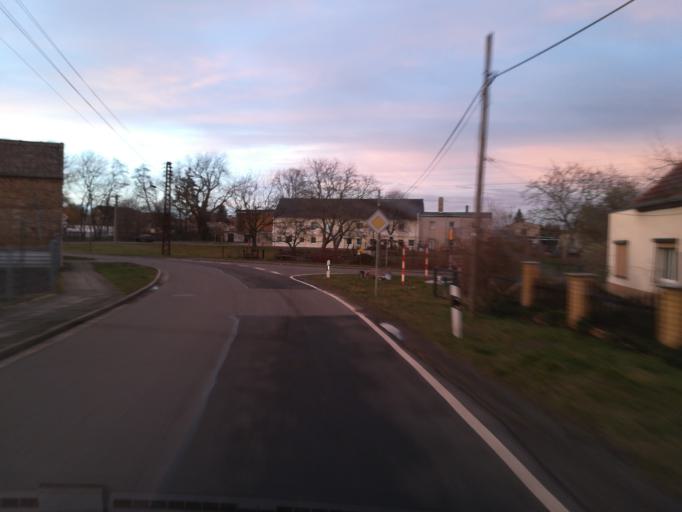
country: DE
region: Saxony-Anhalt
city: Brehna
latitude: 51.5383
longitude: 12.2282
